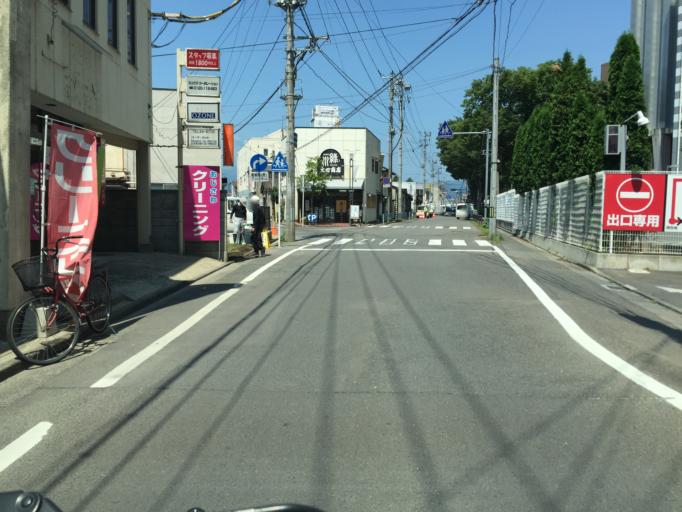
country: JP
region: Fukushima
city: Fukushima-shi
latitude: 37.7520
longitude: 140.4563
